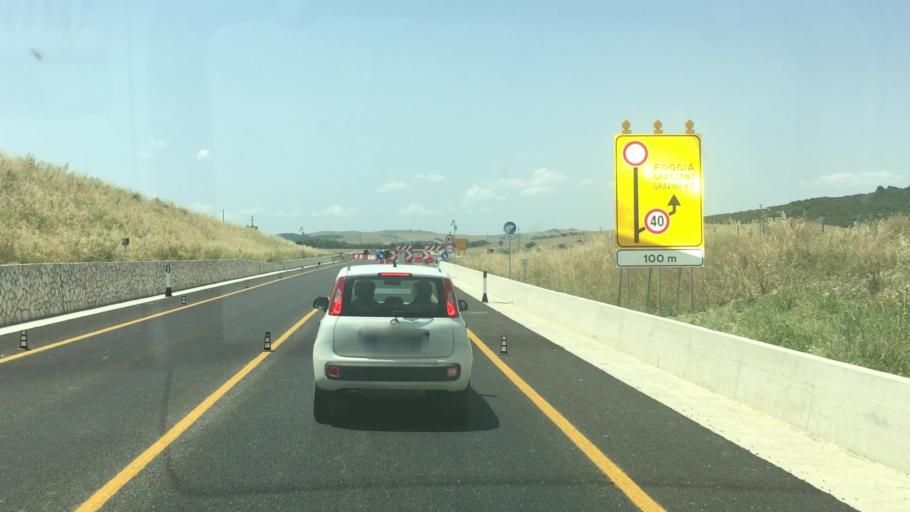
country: IT
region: Basilicate
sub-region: Provincia di Matera
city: La Martella
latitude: 40.6714
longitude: 16.4957
